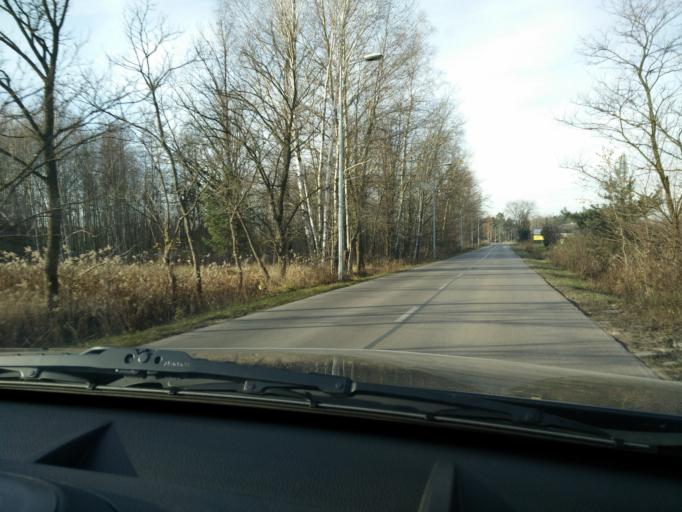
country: PL
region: Masovian Voivodeship
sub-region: Powiat wolominski
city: Duczki
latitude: 52.3104
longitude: 21.3044
